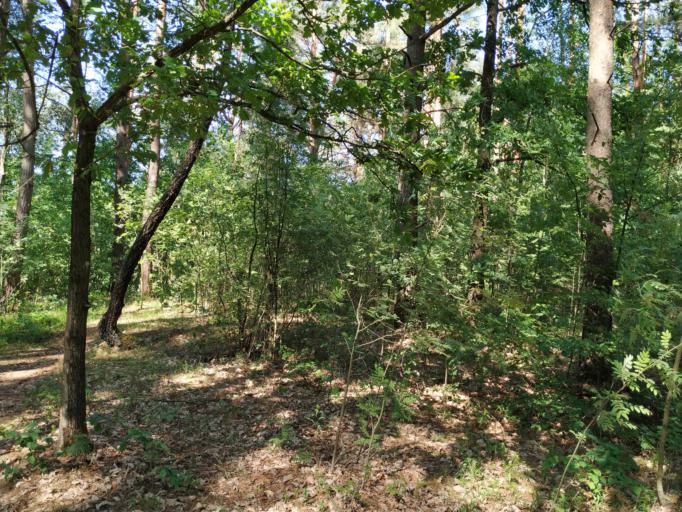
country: LT
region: Vilnius County
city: Rasos
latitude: 54.7616
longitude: 25.3466
